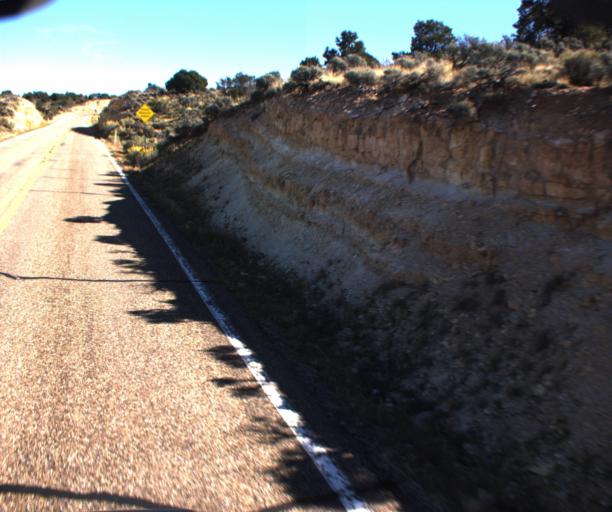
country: US
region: Arizona
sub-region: Coconino County
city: Fredonia
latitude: 36.8469
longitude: -112.2695
